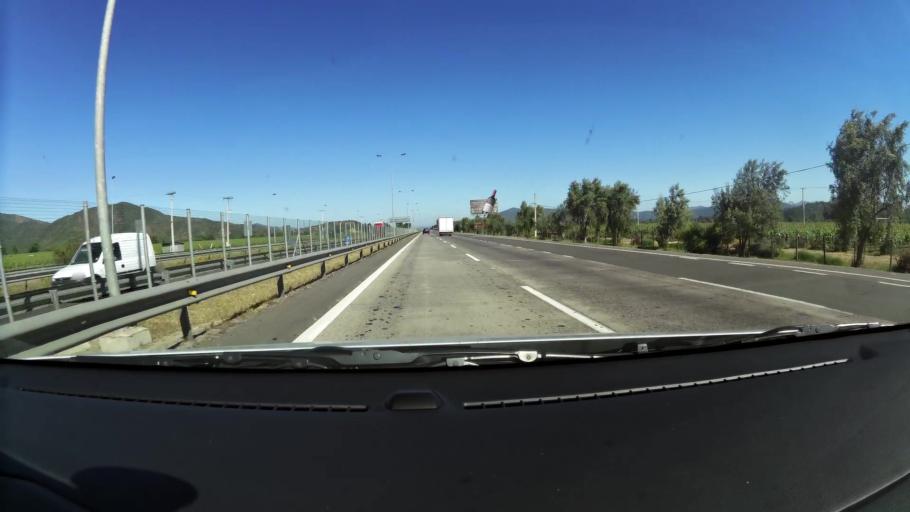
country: CL
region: Valparaiso
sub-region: Provincia de Marga Marga
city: Villa Alemana
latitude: -33.3659
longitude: -71.3098
